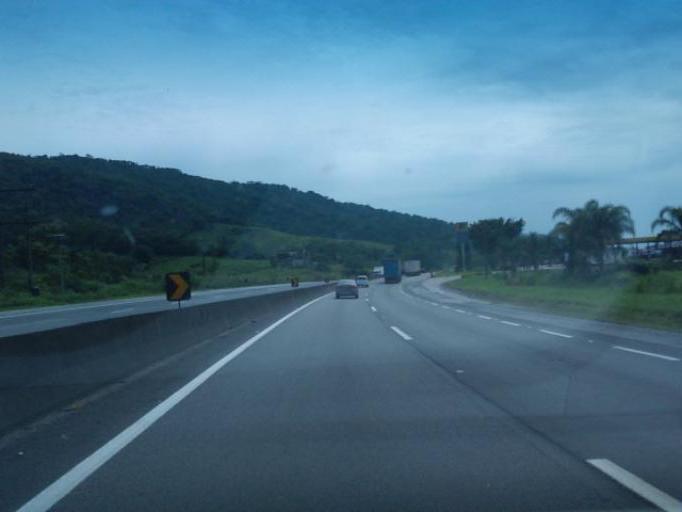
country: BR
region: Sao Paulo
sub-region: Miracatu
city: Miracatu
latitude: -24.3018
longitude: -47.4857
